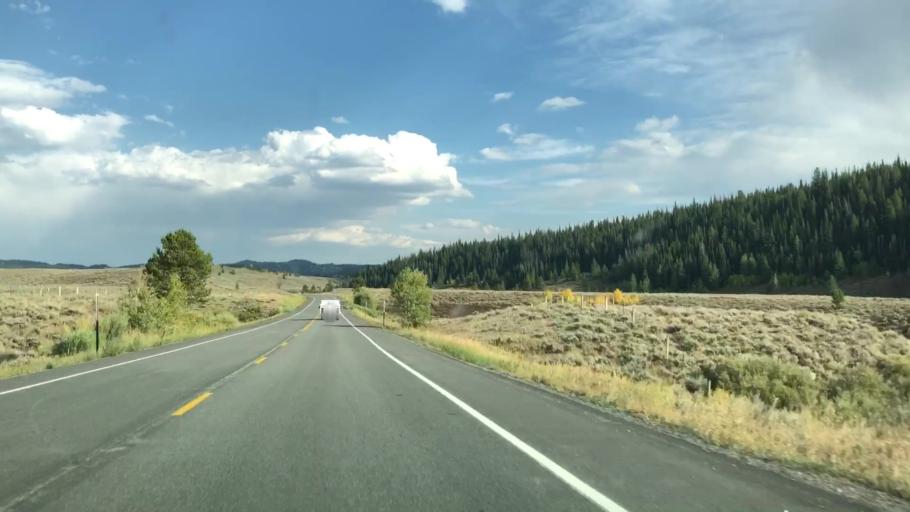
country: US
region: Wyoming
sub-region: Teton County
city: Hoback
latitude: 43.1537
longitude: -110.2954
